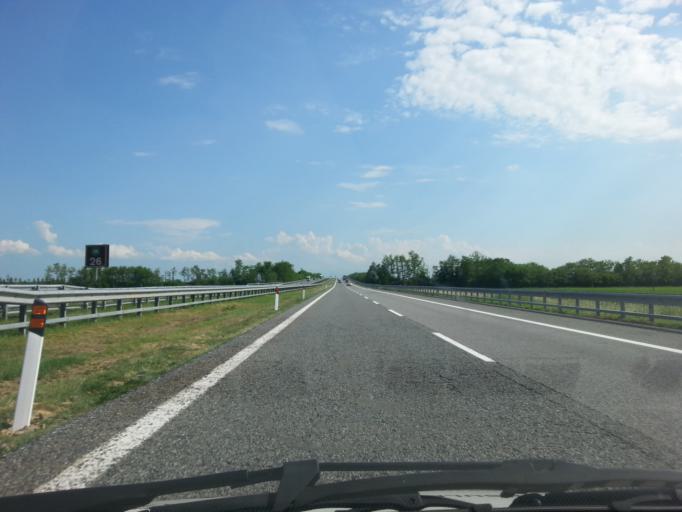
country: IT
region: Piedmont
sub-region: Provincia di Cuneo
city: Caramagna Piemonte
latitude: 44.8153
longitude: 7.7511
